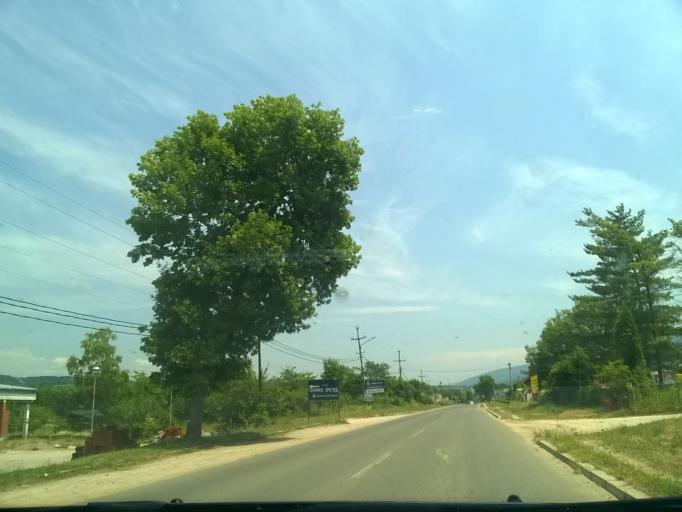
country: RS
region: Central Serbia
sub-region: Zajecarski Okrug
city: Soko Banja
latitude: 43.6517
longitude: 21.8499
